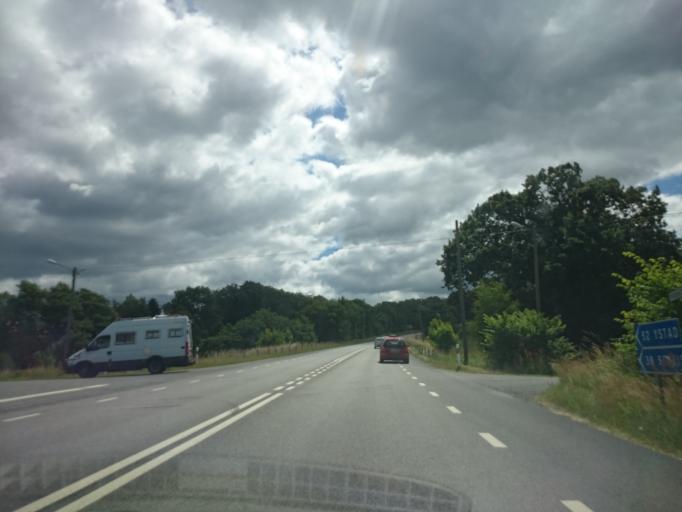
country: SE
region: Skane
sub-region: Kristianstads Kommun
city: Degeberga
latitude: 55.8046
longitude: 14.1470
